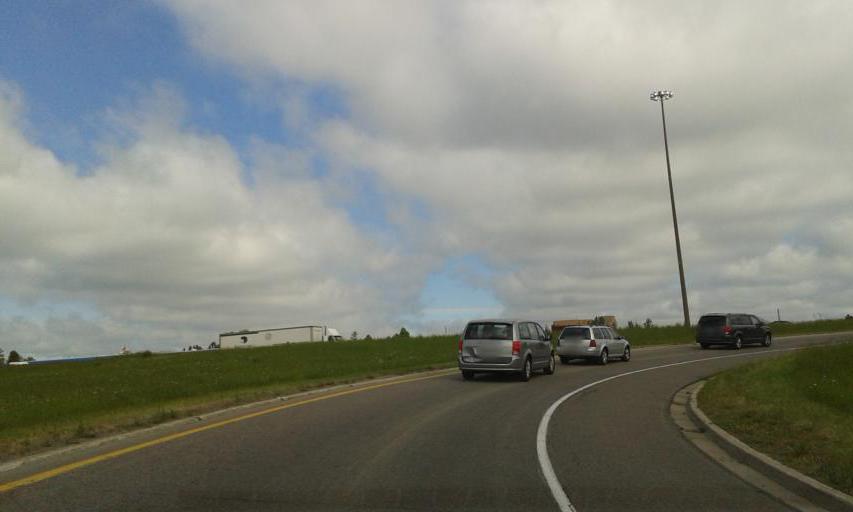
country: CA
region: Ontario
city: Scarborough
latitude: 43.7840
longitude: -79.2360
